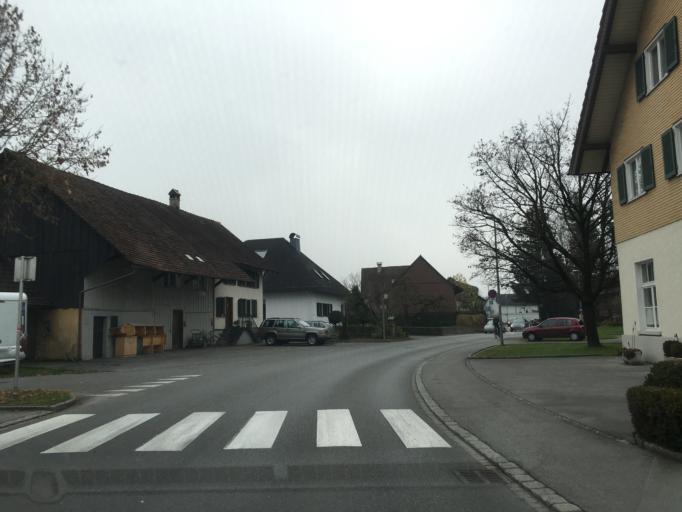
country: AT
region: Vorarlberg
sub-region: Politischer Bezirk Dornbirn
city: Lustenau
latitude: 47.4292
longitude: 9.6640
